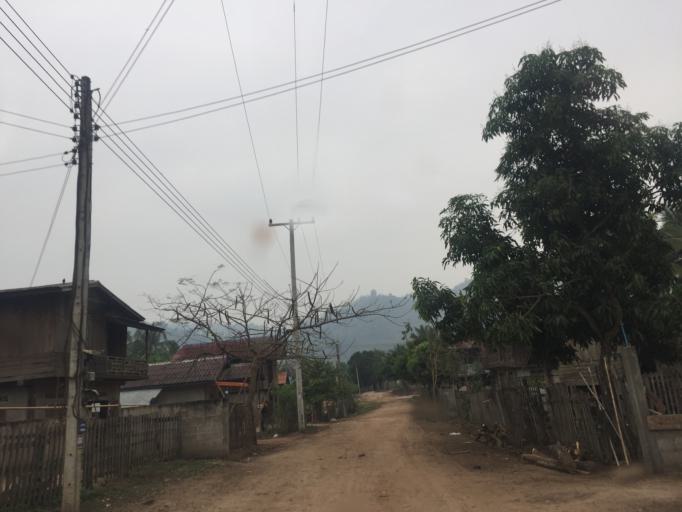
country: LA
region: Xiagnabouli
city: Sainyabuli
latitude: 18.9806
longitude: 101.4841
